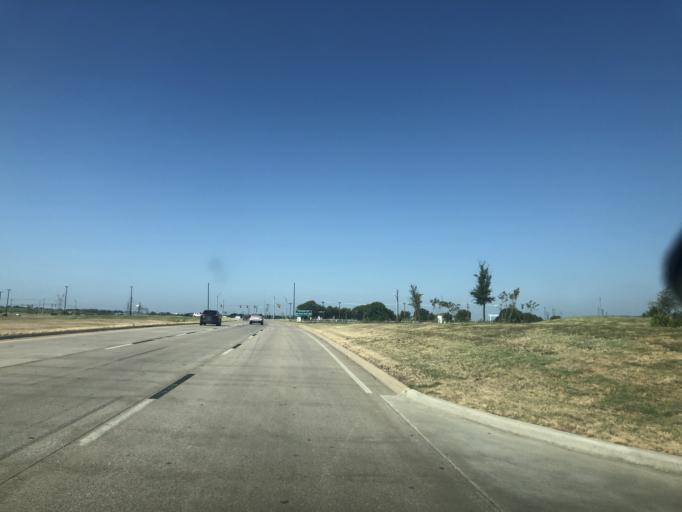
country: US
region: Texas
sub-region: Tarrant County
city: Haslet
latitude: 32.9664
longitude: -97.2956
